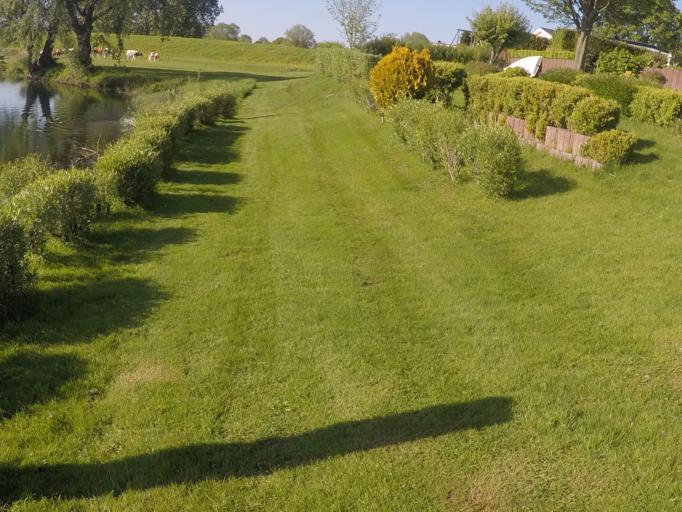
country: NL
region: Gelderland
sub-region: Gemeente Rheden
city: Rheden
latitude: 51.9945
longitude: 6.0232
